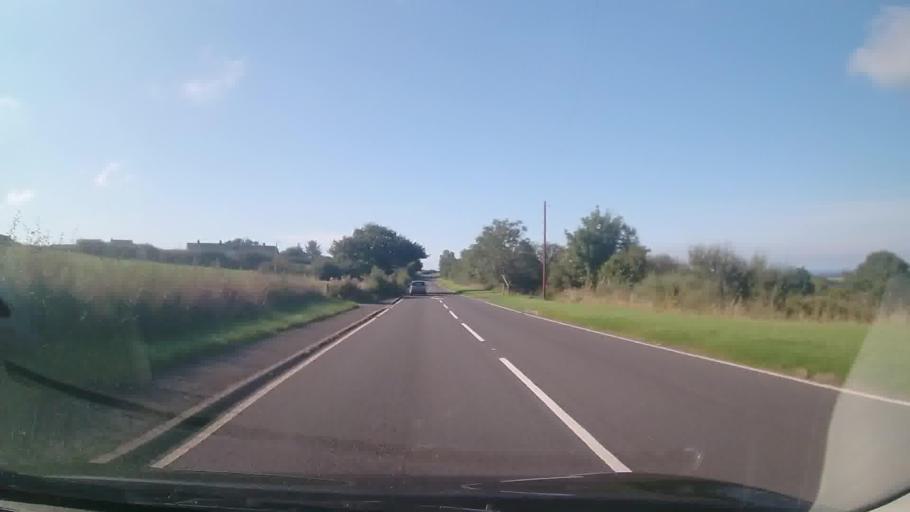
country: GB
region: England
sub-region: Cumbria
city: Seascale
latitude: 54.3352
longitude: -3.3664
